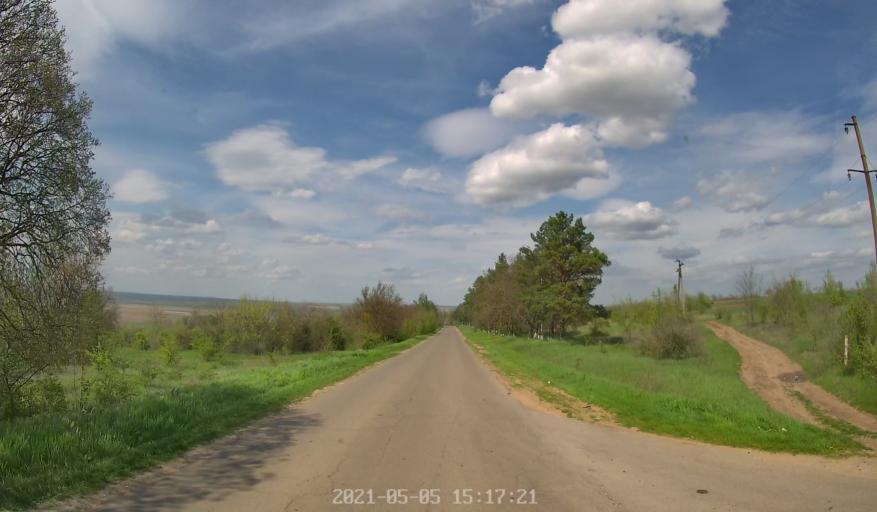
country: MD
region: Criuleni
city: Criuleni
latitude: 47.1110
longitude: 29.1937
